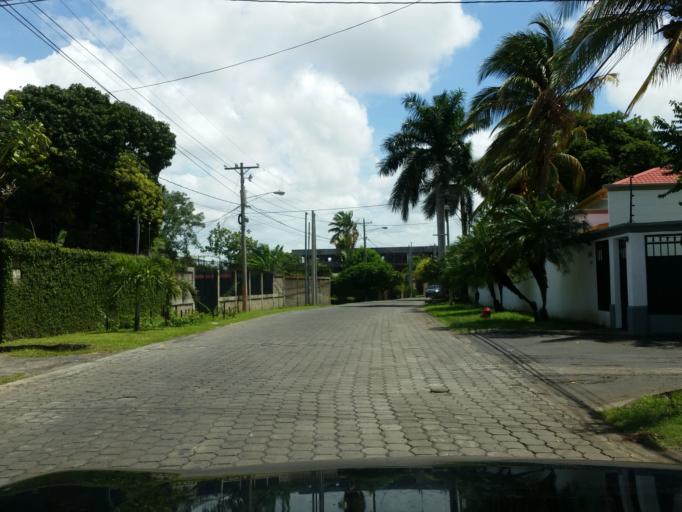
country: NI
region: Managua
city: Managua
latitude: 12.0847
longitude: -86.2325
